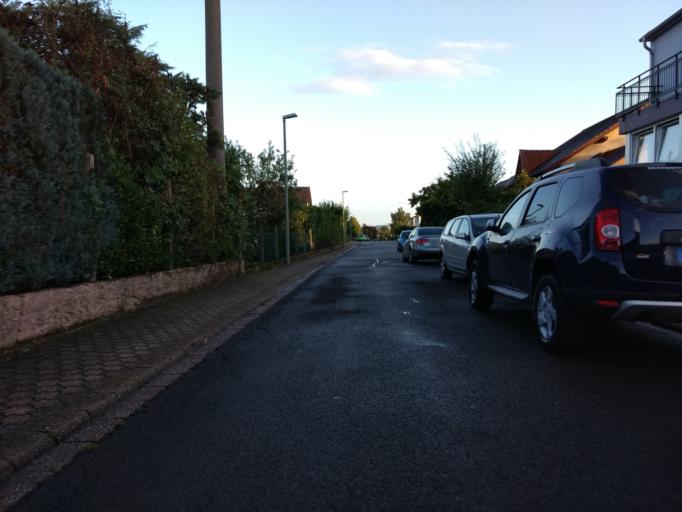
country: DE
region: Saarland
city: Nalbach
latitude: 49.3839
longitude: 6.7552
